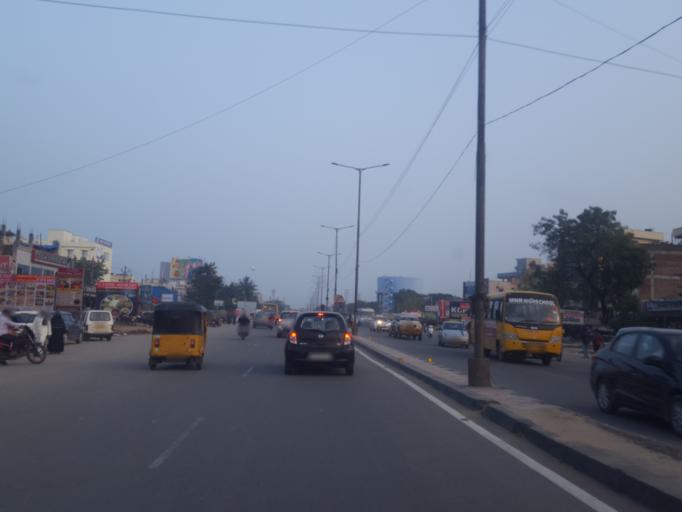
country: IN
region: Telangana
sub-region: Medak
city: Serilingampalle
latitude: 17.5086
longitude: 78.3012
